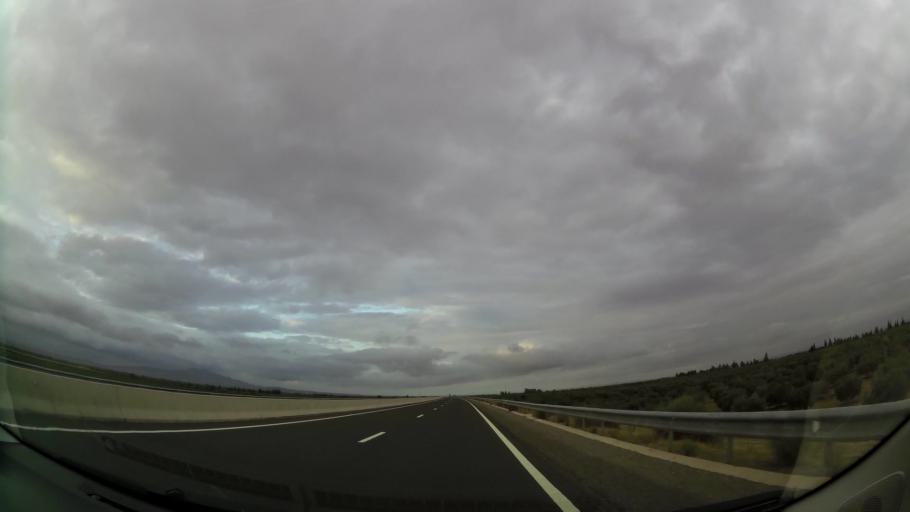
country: MA
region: Taza-Al Hoceima-Taounate
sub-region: Taza
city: Guercif
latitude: 34.3327
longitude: -3.3369
